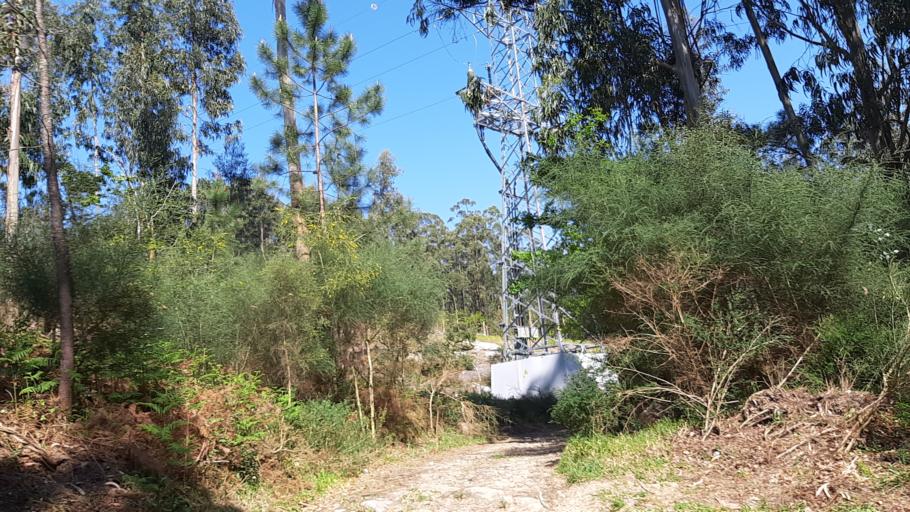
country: ES
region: Galicia
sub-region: Provincia de Pontevedra
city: O Rosal
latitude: 41.9394
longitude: -8.8547
